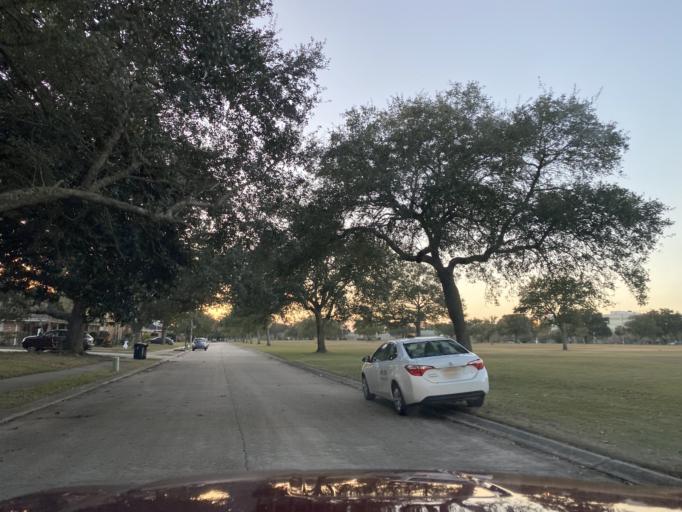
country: US
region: Louisiana
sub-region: Orleans Parish
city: New Orleans
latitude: 30.0297
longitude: -90.0555
